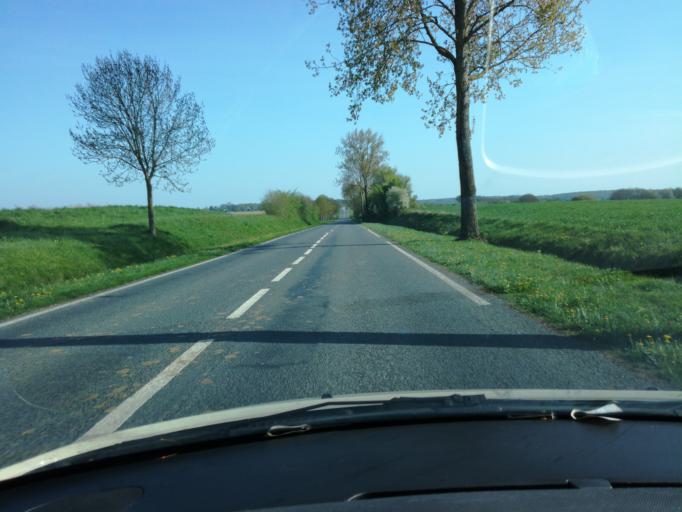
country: FR
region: Picardie
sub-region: Departement de la Somme
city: Poix-de-Picardie
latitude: 49.8055
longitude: 1.9684
